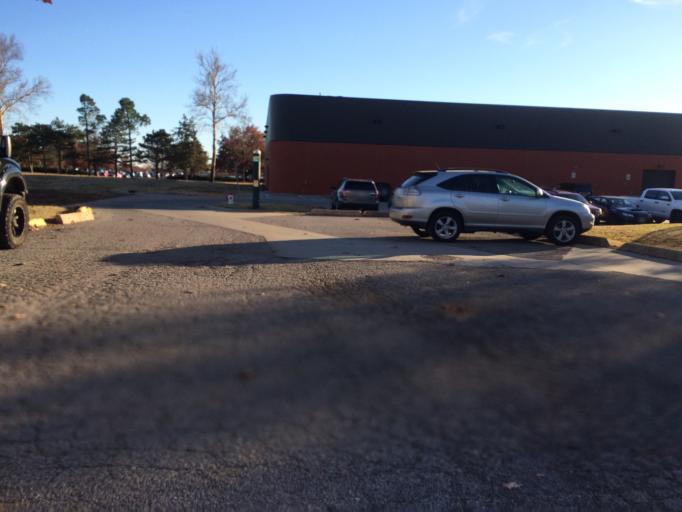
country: US
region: Oklahoma
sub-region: Cleveland County
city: Norman
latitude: 35.1911
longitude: -97.4436
